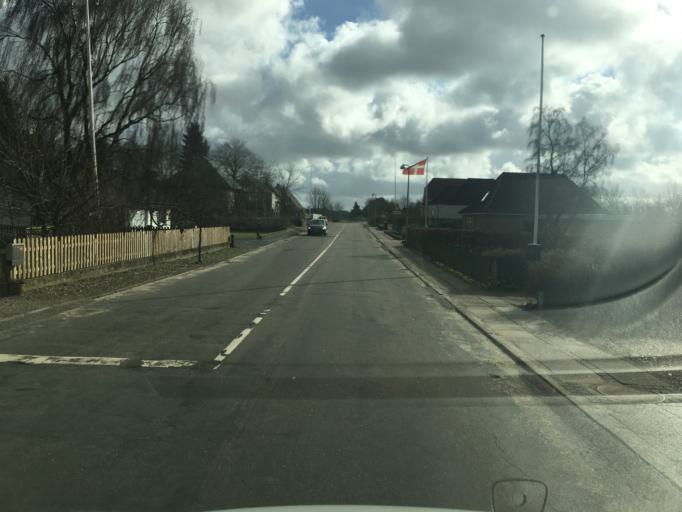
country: DK
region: South Denmark
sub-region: Aabenraa Kommune
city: Tinglev
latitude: 54.9323
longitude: 9.3297
